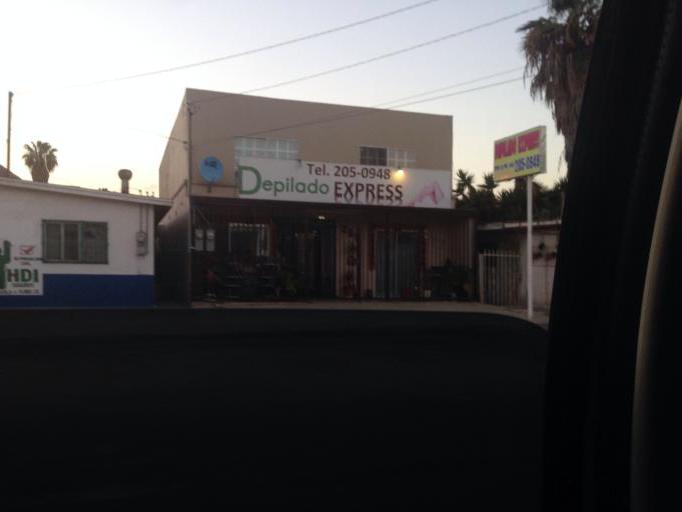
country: MX
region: Baja California
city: Ensenada
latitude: 31.8588
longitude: -116.6115
